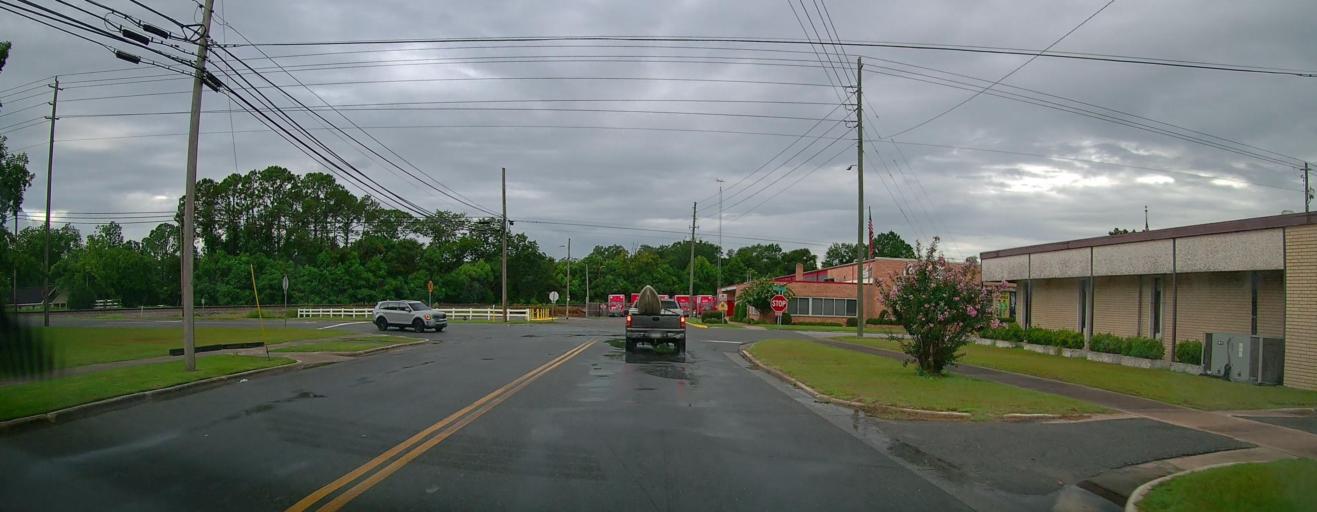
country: US
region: Georgia
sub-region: Ware County
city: Waycross
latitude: 31.2081
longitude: -82.3654
